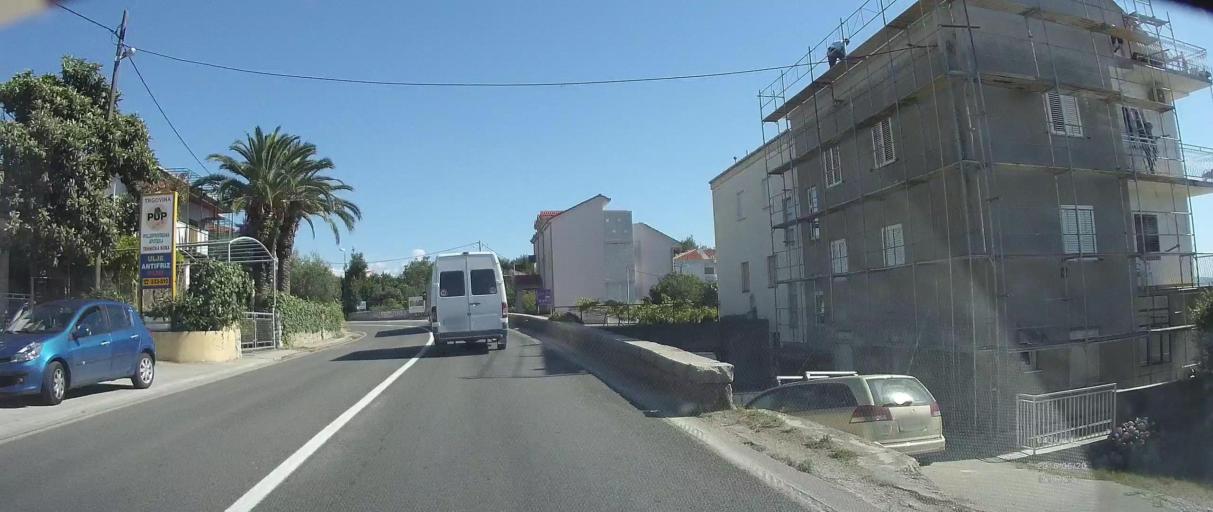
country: HR
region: Splitsko-Dalmatinska
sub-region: Grad Split
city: Stobrec
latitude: 43.4966
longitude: 16.5371
